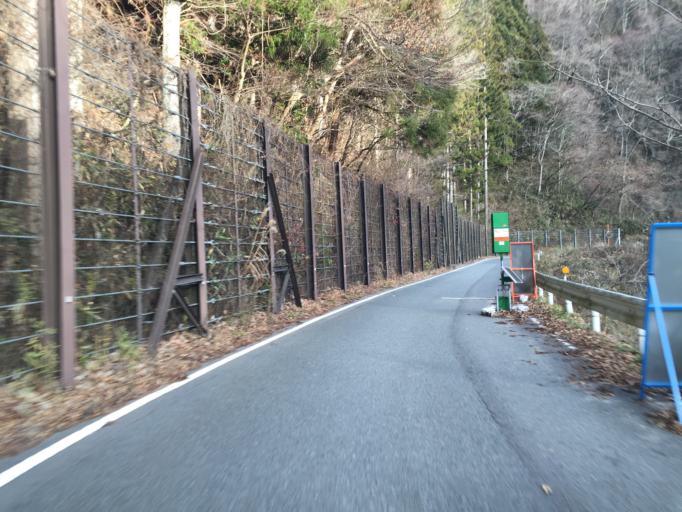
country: JP
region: Fukushima
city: Funehikimachi-funehiki
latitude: 37.2367
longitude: 140.6886
